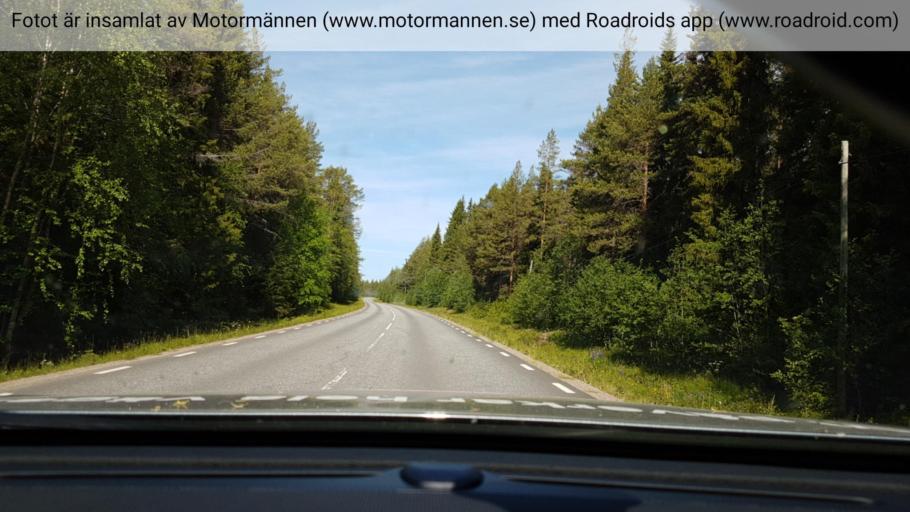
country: SE
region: Vaesterbotten
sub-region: Dorotea Kommun
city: Dorotea
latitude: 64.2626
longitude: 16.3665
